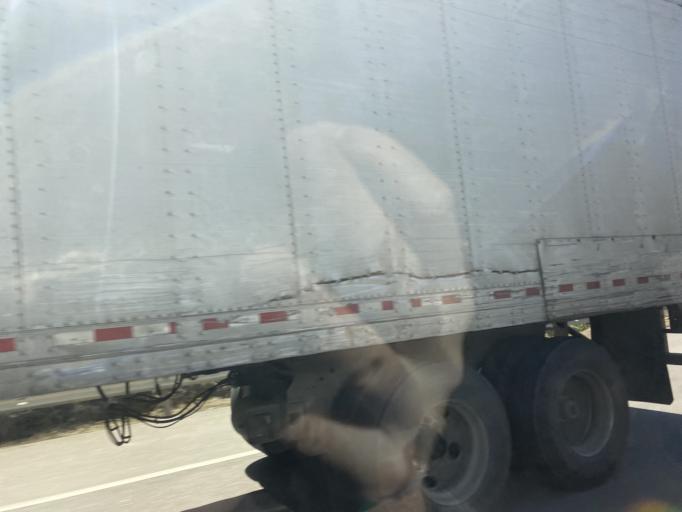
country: DO
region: Puerto Plata
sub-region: Puerto Plata
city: Puerto Plata
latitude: 19.8302
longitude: -70.7652
